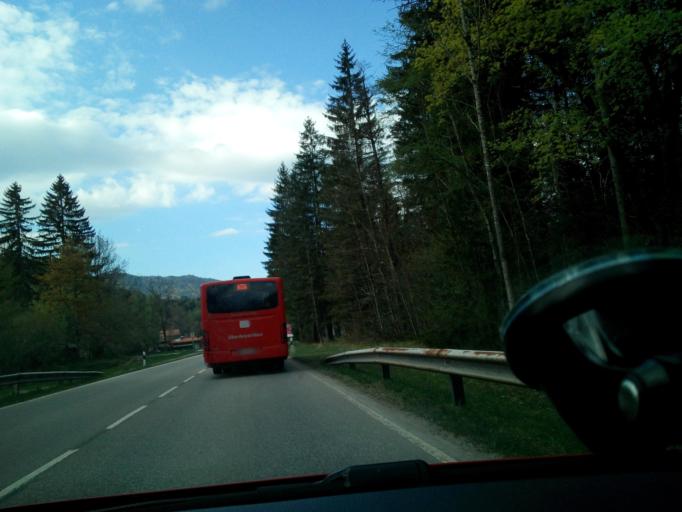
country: DE
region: Bavaria
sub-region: Upper Bavaria
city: Kreuth
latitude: 47.6389
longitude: 11.7450
